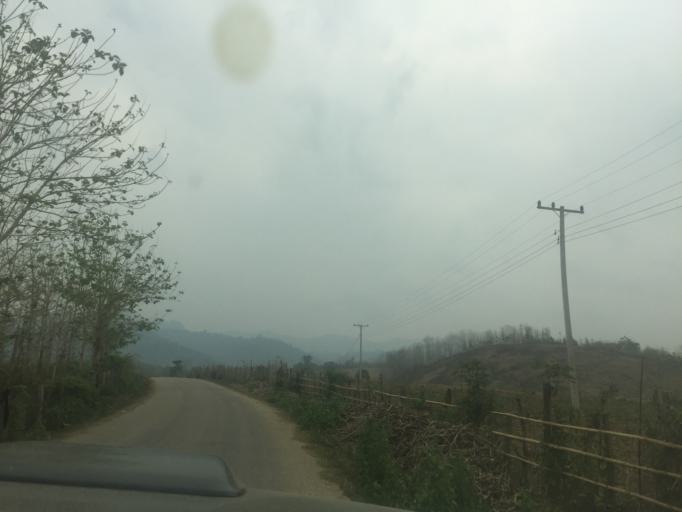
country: LA
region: Vientiane
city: Muang Sanakham
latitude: 18.3788
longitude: 101.5478
